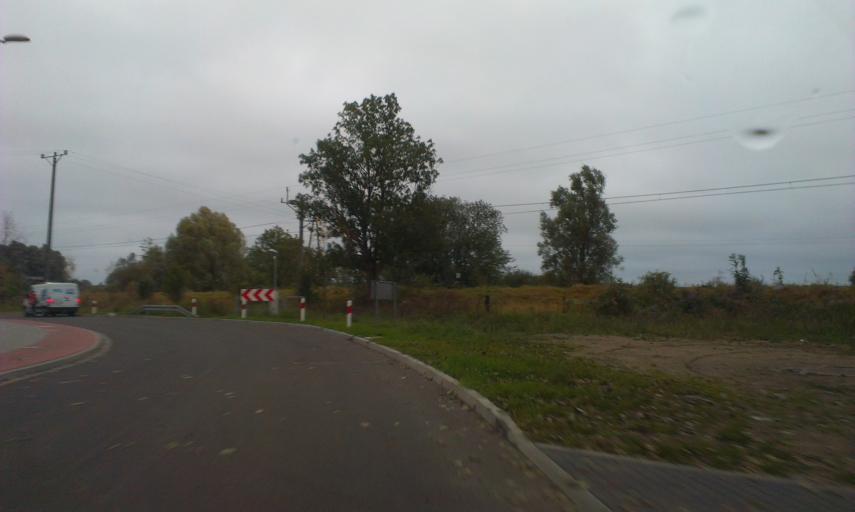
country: PL
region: West Pomeranian Voivodeship
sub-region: Powiat szczecinecki
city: Szczecinek
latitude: 53.7207
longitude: 16.6895
